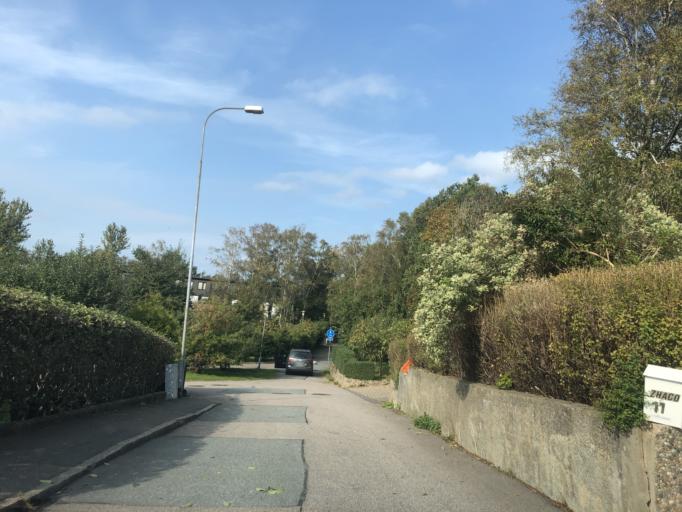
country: SE
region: Vaestra Goetaland
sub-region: Goteborg
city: Majorna
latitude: 57.6517
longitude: 11.8945
